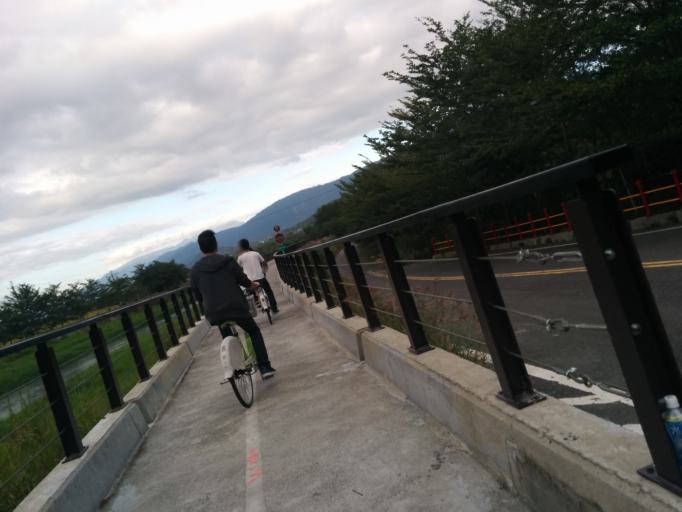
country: TW
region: Taiwan
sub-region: Taitung
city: Taitung
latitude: 23.0264
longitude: 121.1638
